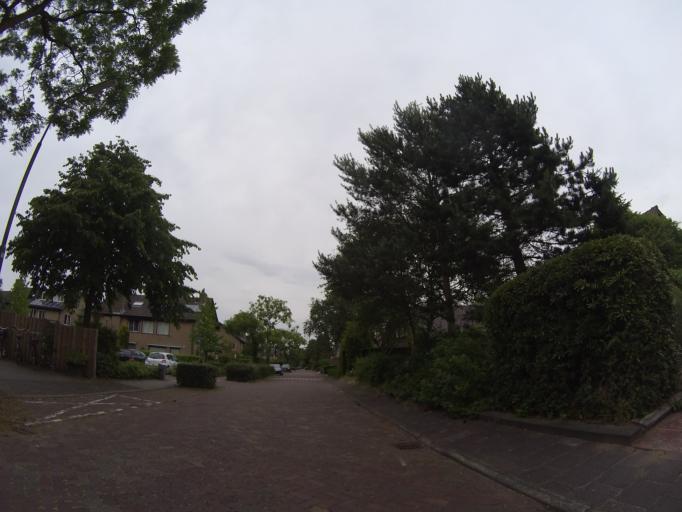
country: NL
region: Utrecht
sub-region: Gemeente Leusden
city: Leusden
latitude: 52.1333
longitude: 5.4310
